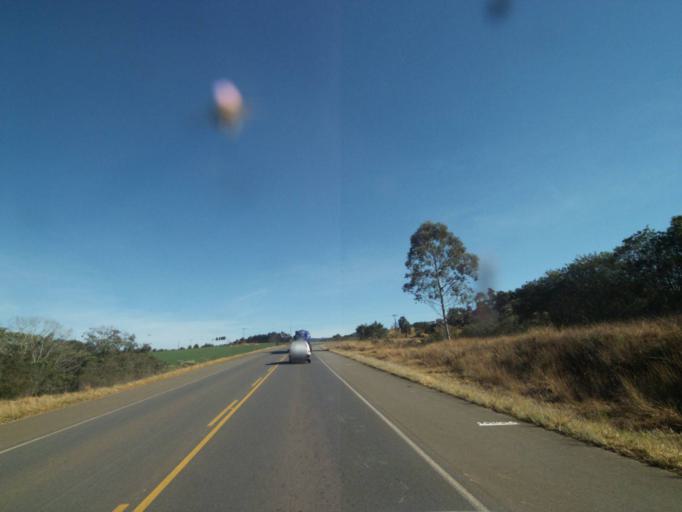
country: BR
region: Parana
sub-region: Tibagi
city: Tibagi
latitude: -24.5247
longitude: -50.4421
